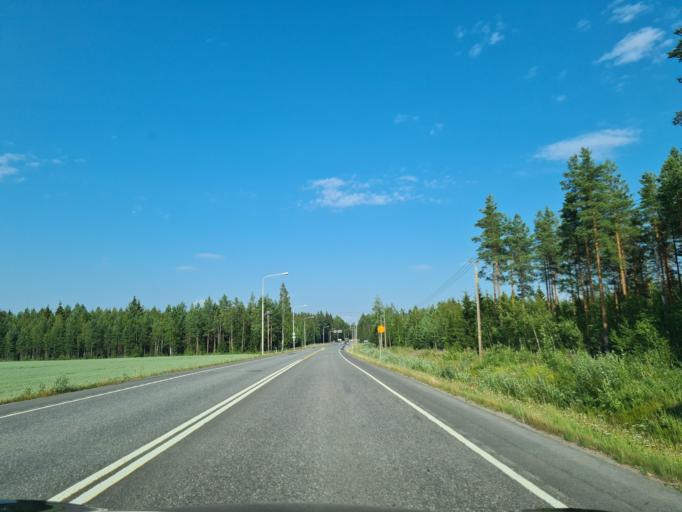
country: FI
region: Satakunta
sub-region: Pohjois-Satakunta
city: Kankaanpaeae
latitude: 61.8302
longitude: 22.3980
